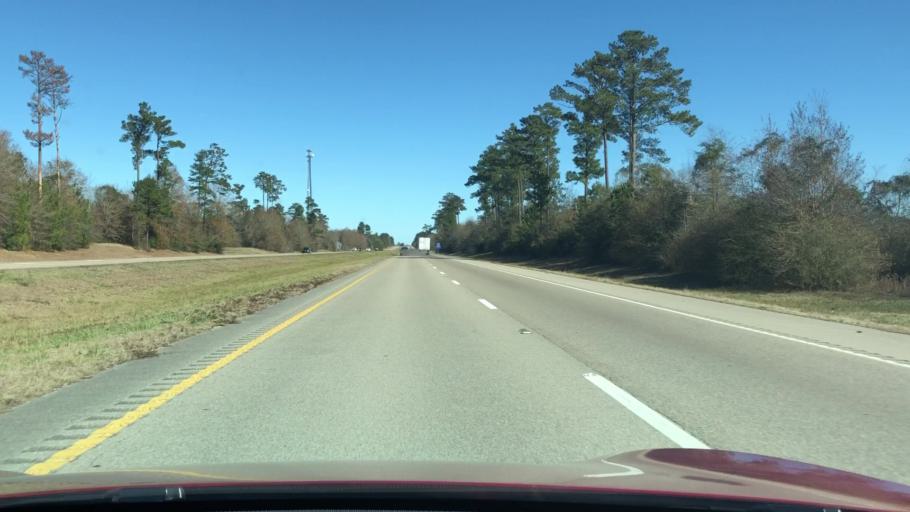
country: US
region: Mississippi
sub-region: Pearl River County
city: Poplarville
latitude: 30.7290
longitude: -89.5475
